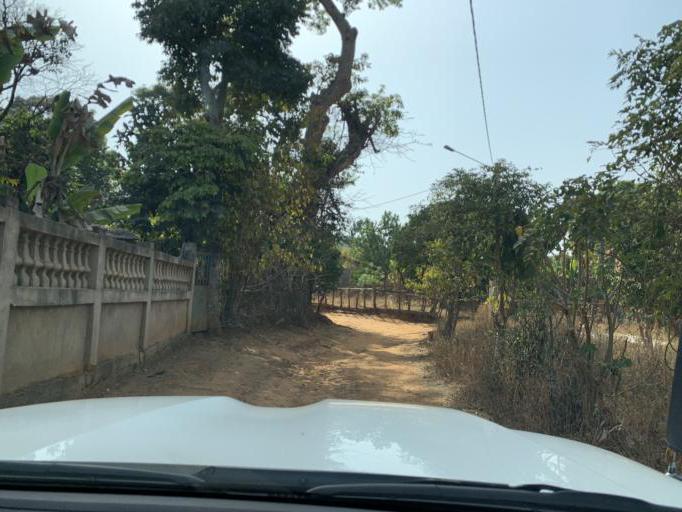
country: GN
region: Mamou
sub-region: Dalaba
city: Dalaba
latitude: 10.7657
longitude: -12.2824
